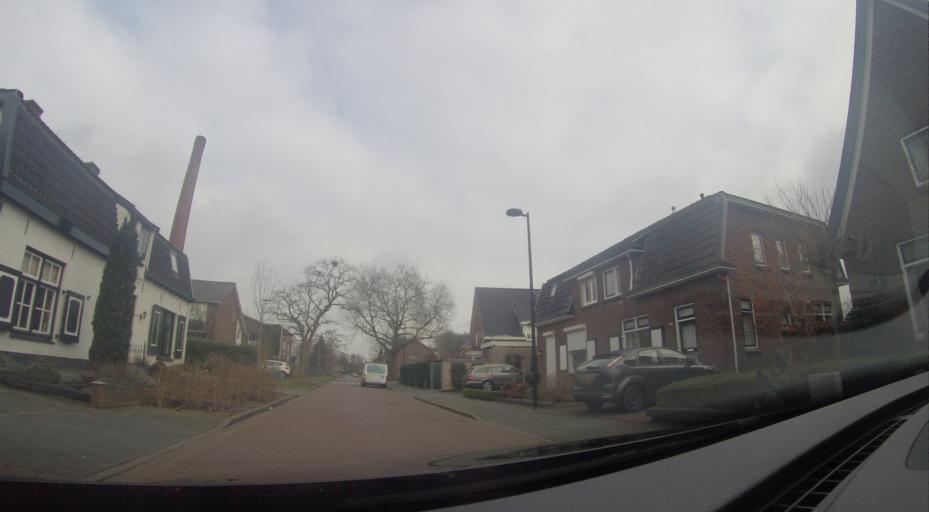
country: NL
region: Gelderland
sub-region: Gemeente Doetinchem
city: Doetinchem
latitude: 51.9679
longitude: 6.2801
